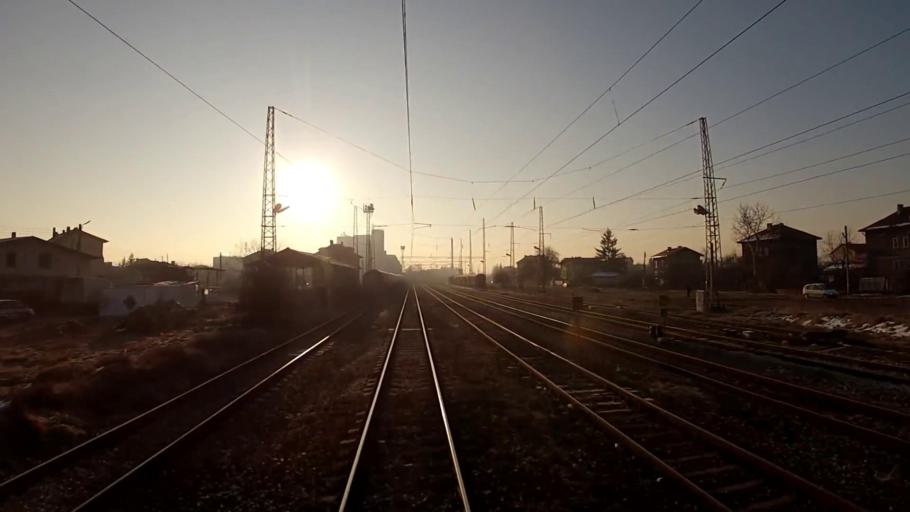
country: BG
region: Sofiya
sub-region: Obshtina Kostinbrod
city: Kostinbrod
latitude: 42.8012
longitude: 23.2038
